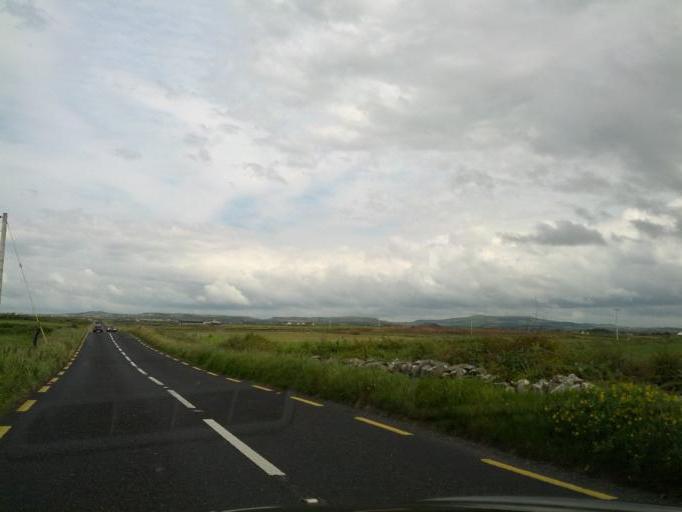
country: IE
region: Munster
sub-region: An Clar
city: Kilrush
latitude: 52.8241
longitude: -9.4455
